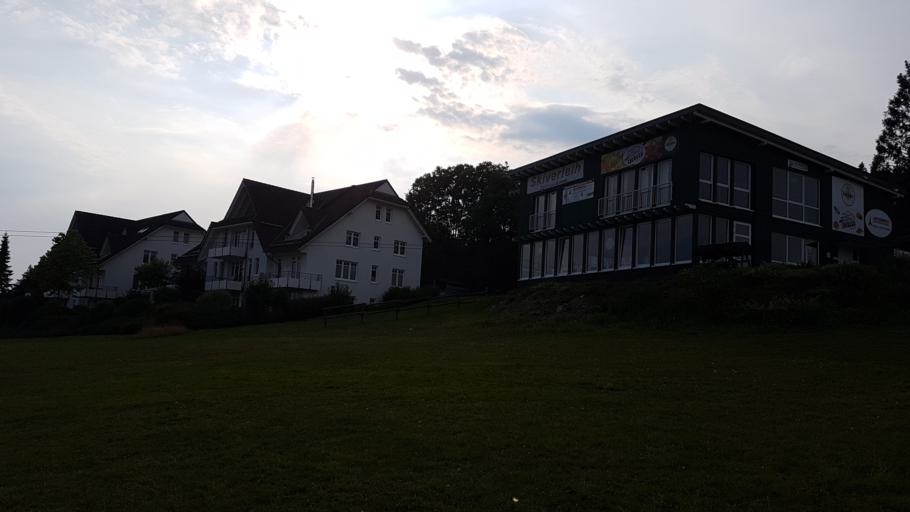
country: DE
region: North Rhine-Westphalia
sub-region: Regierungsbezirk Arnsberg
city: Winterberg
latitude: 51.1645
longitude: 8.4871
